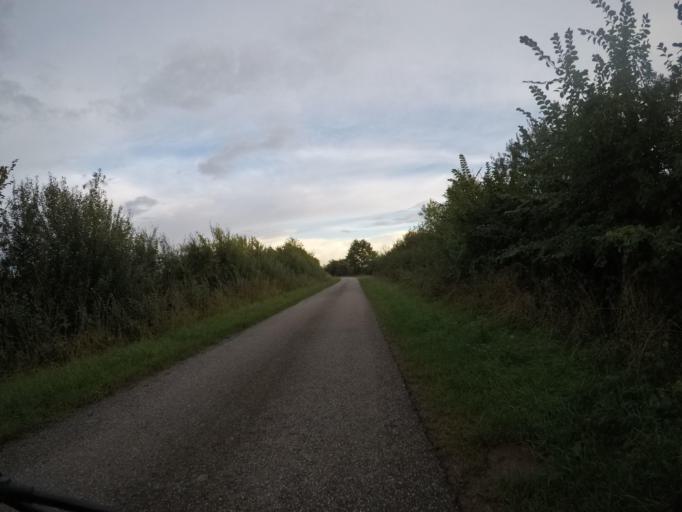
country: DE
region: Lower Saxony
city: Neu Darchau
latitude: 53.2646
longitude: 10.9044
